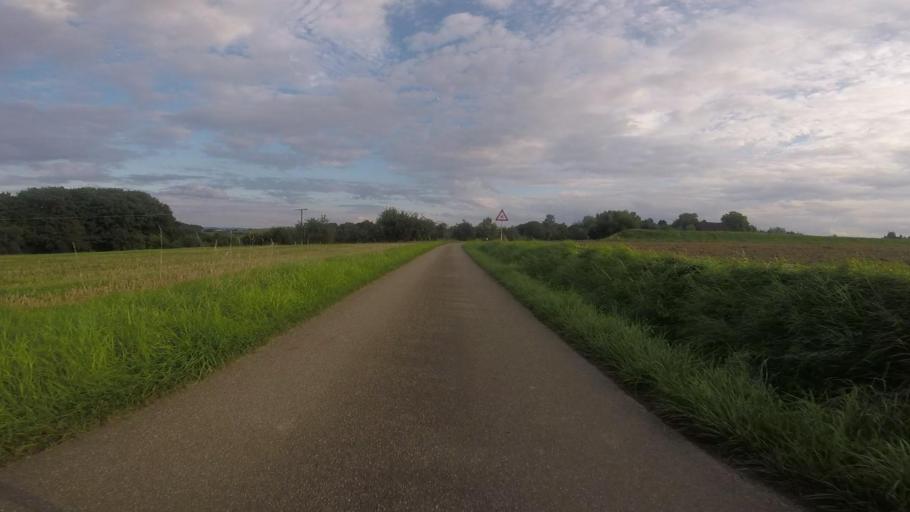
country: DE
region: Baden-Wuerttemberg
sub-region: Regierungsbezirk Stuttgart
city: Oberstenfeld
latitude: 49.0110
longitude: 9.3605
